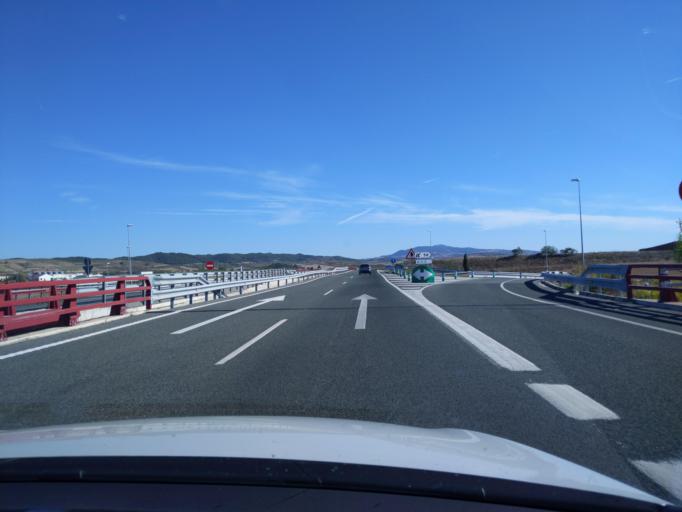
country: ES
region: Navarre
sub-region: Provincia de Navarra
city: Los Arcos
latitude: 42.5580
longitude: -2.1848
